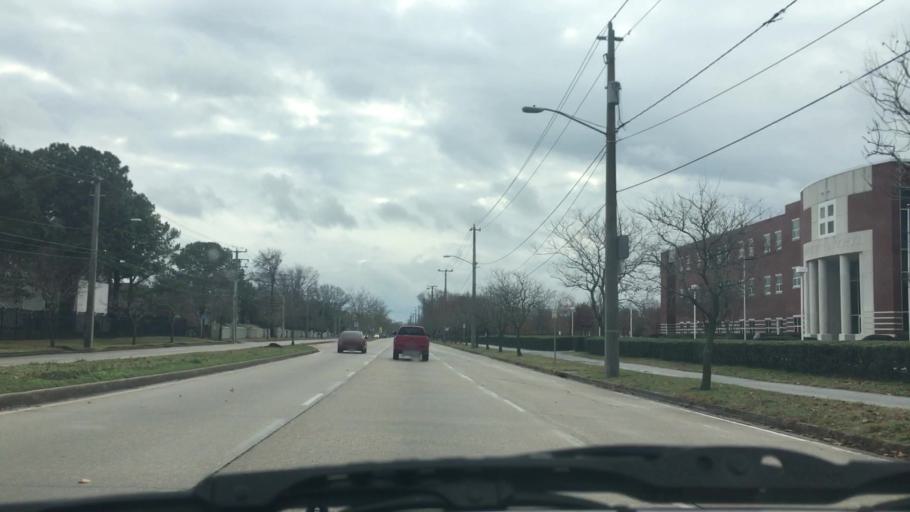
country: US
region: Virginia
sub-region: City of Norfolk
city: Norfolk
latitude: 36.9009
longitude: -76.2394
